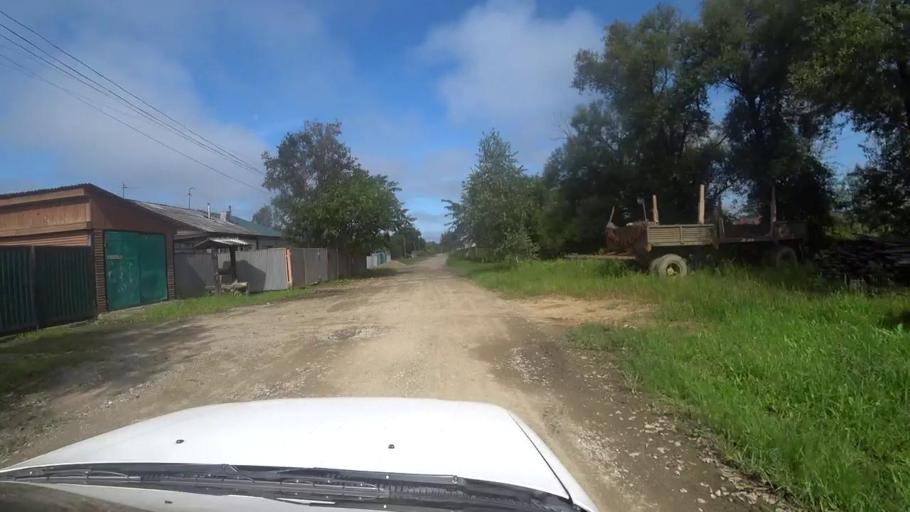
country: RU
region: Primorskiy
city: Dal'nerechensk
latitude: 45.9178
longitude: 133.7246
